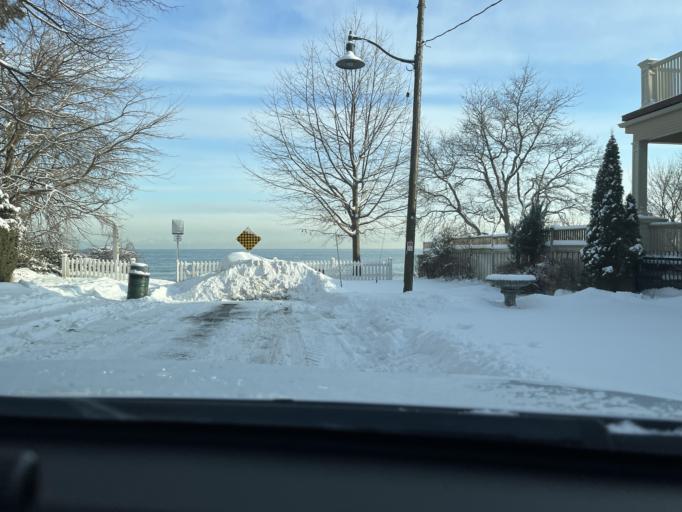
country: CA
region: Ontario
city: Oakville
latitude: 43.4457
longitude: -79.6636
